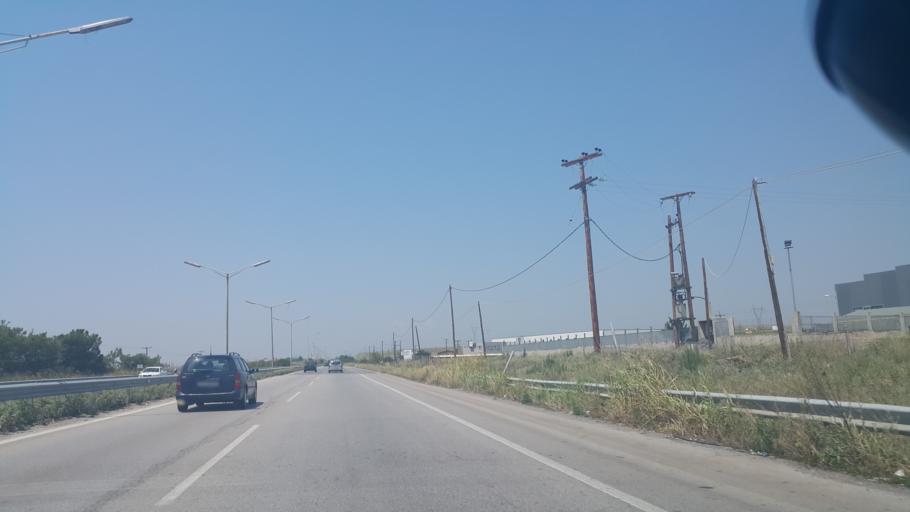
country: GR
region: Central Macedonia
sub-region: Nomos Thessalonikis
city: Agios Athanasios
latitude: 40.7125
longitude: 22.7536
